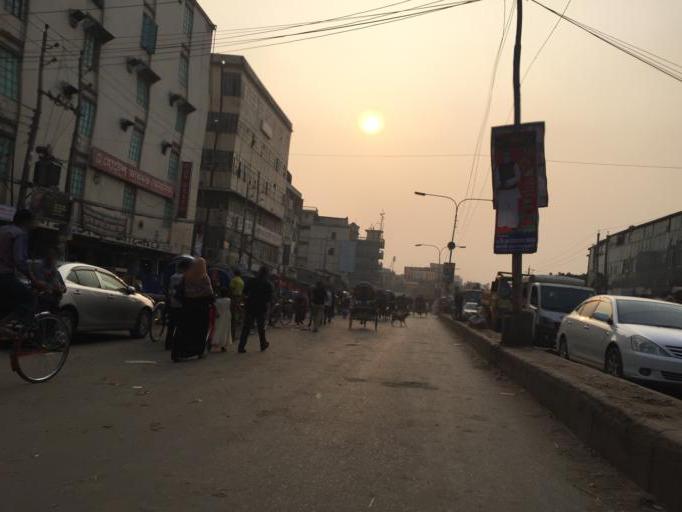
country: BD
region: Dhaka
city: Azimpur
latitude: 23.7971
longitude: 90.3507
